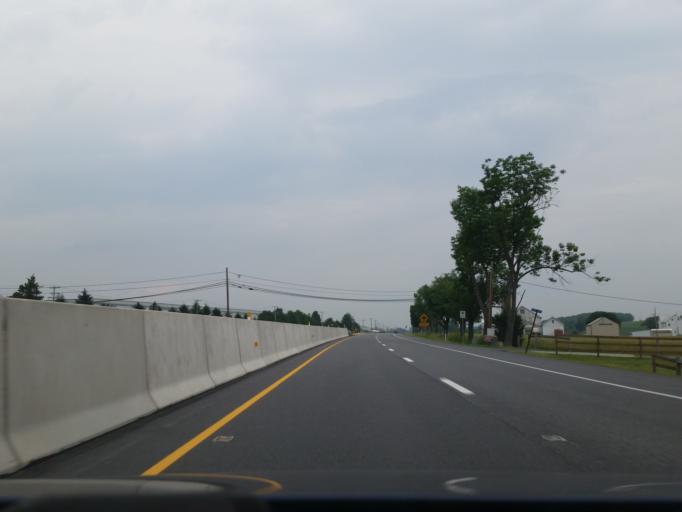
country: US
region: Pennsylvania
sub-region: Lebanon County
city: Fredericksburg
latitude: 40.4422
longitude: -76.4240
